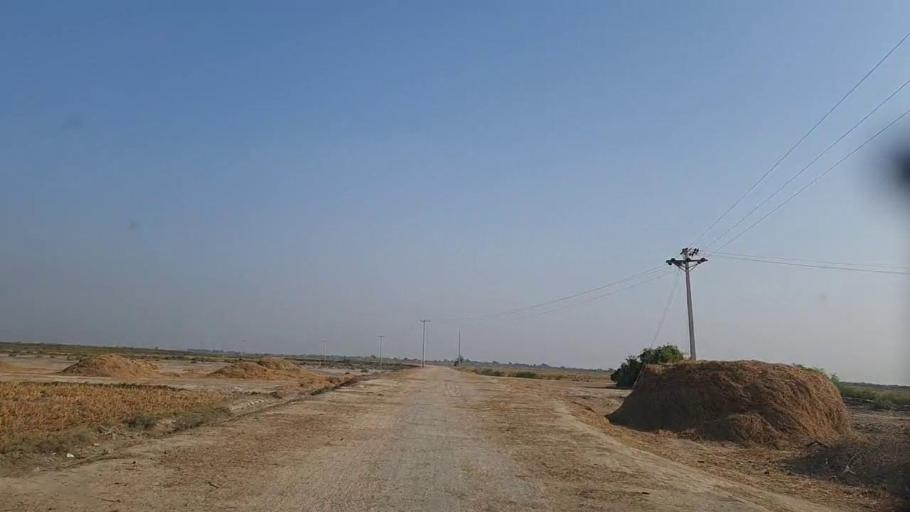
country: PK
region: Sindh
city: Jati
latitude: 24.4625
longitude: 68.2762
